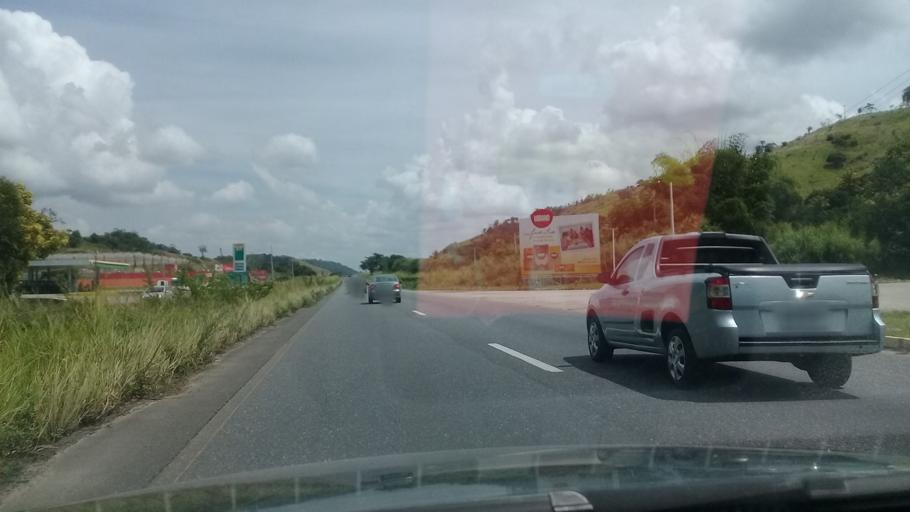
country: BR
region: Pernambuco
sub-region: Vitoria De Santo Antao
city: Vitoria de Santo Antao
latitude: -8.1135
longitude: -35.2123
